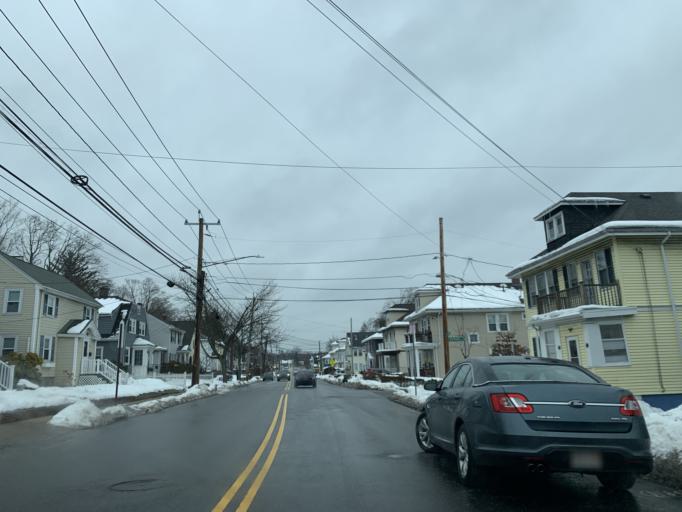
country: US
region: Massachusetts
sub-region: Norfolk County
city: Dedham
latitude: 42.2864
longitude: -71.1644
